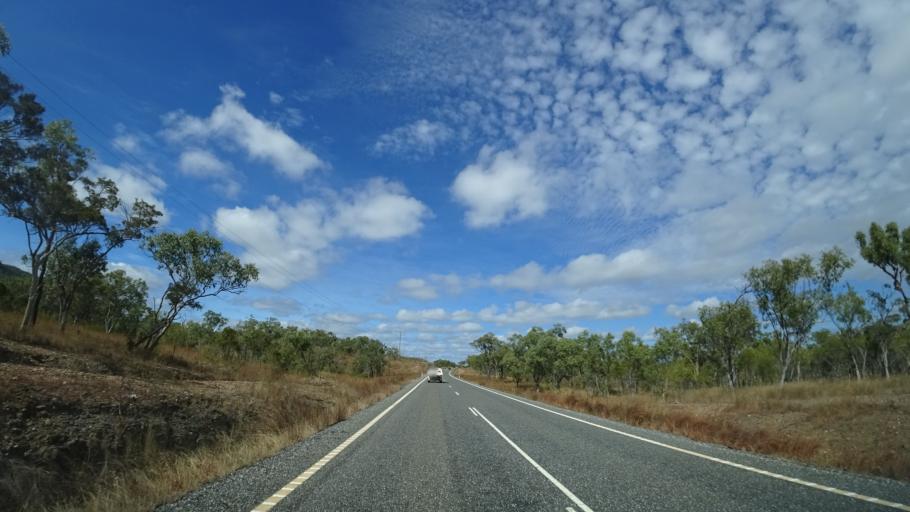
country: AU
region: Queensland
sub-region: Cairns
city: Port Douglas
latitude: -16.3747
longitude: 144.7350
